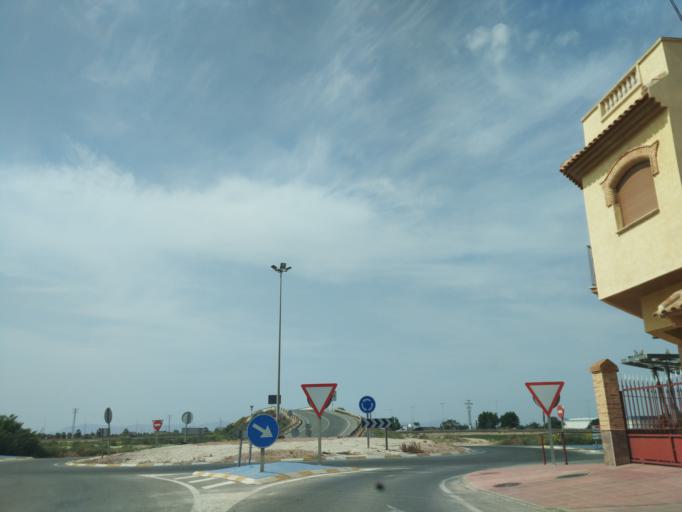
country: ES
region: Murcia
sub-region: Murcia
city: Torre-Pacheco
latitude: 37.8181
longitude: -0.9631
